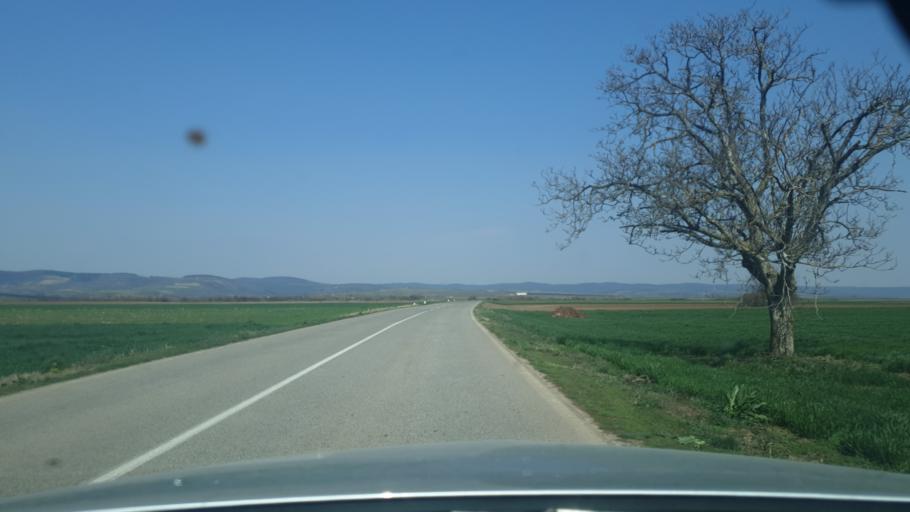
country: RS
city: Vrdnik
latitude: 45.0643
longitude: 19.7689
